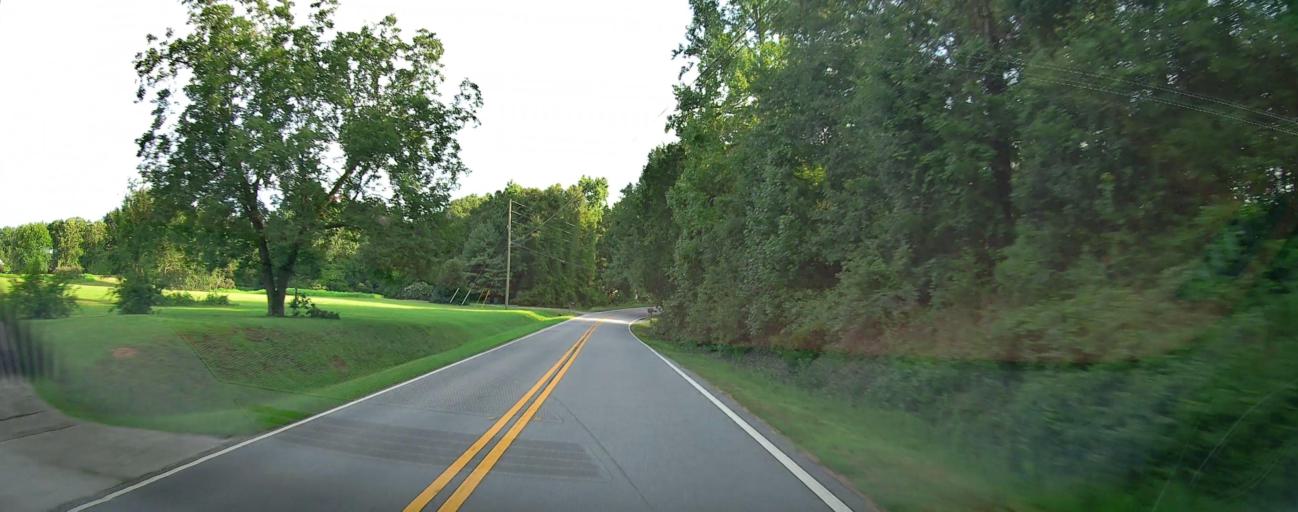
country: US
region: Georgia
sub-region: Peach County
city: Byron
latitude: 32.7311
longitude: -83.7413
